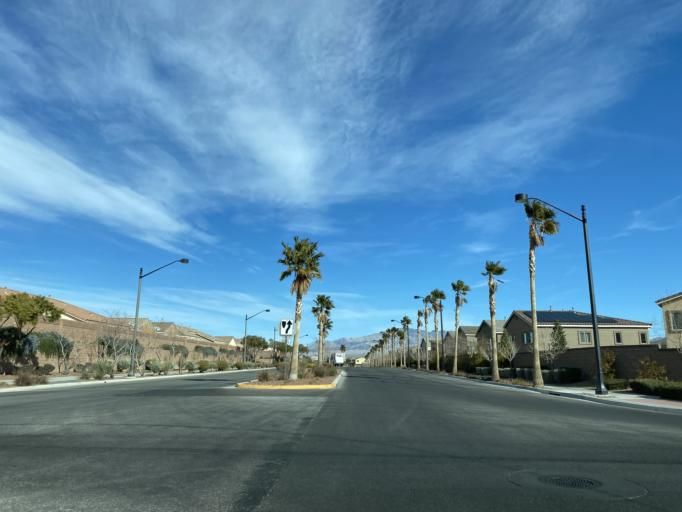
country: US
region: Nevada
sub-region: Clark County
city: Summerlin South
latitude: 36.3029
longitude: -115.2968
